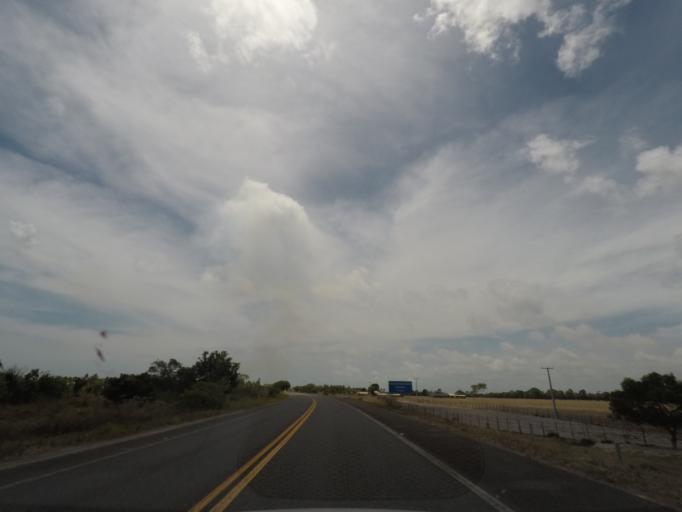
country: BR
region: Bahia
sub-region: Conde
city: Conde
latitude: -11.7486
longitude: -37.5857
